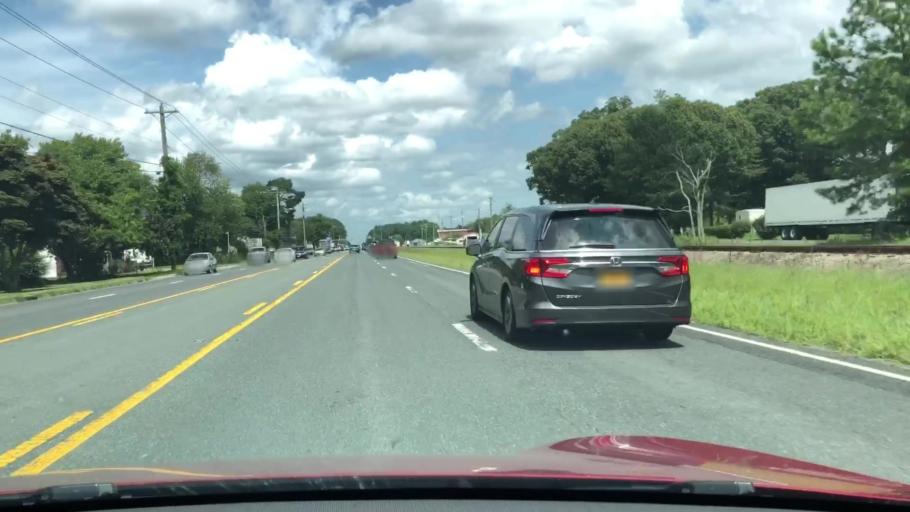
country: US
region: Virginia
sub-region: Accomack County
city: Onancock
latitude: 37.6462
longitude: -75.7449
